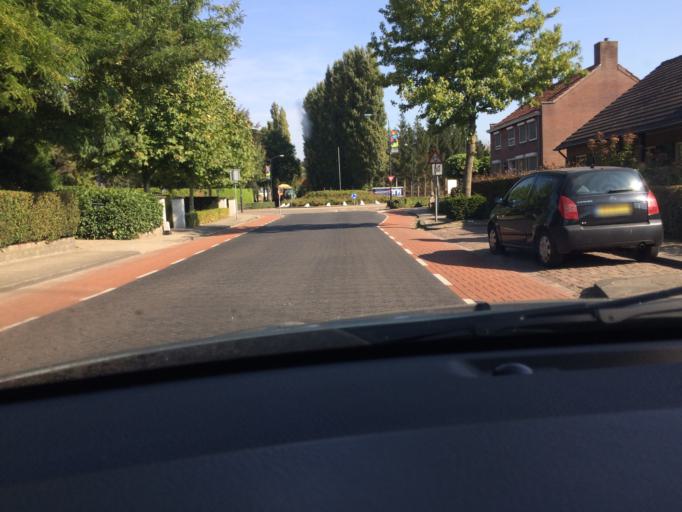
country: NL
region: North Brabant
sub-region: Gemeente Baarle-Nassau
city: Baarle-Nassau
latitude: 51.4462
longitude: 4.9354
